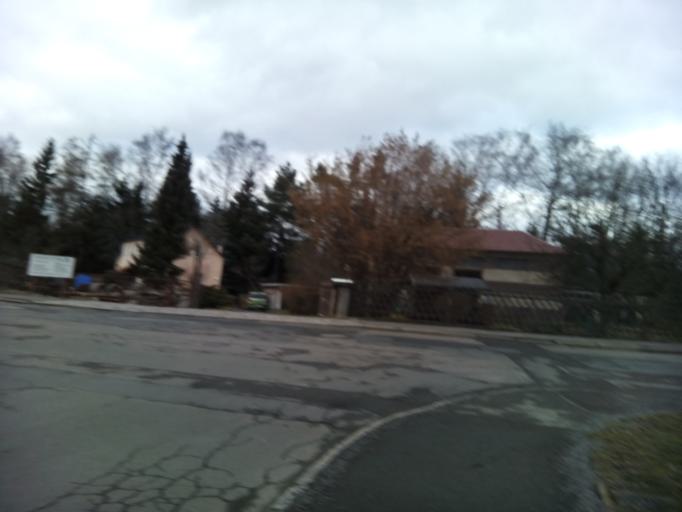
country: DE
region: Saxony
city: Freiberg
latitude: 50.9093
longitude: 13.3299
